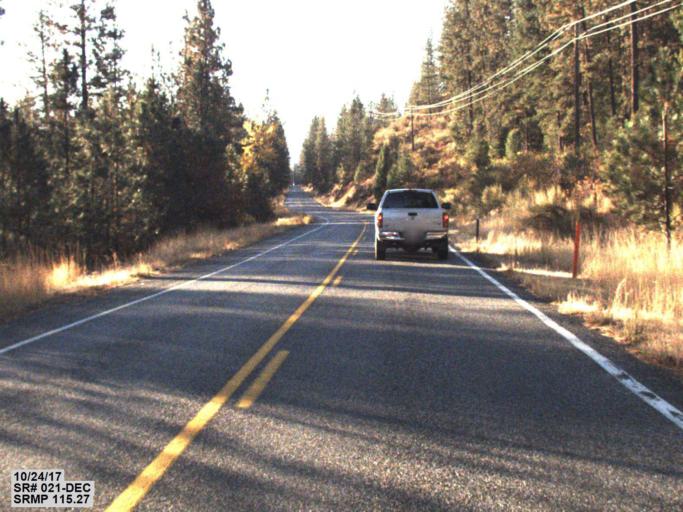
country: US
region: Washington
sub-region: Okanogan County
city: Coulee Dam
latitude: 48.0603
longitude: -118.6731
